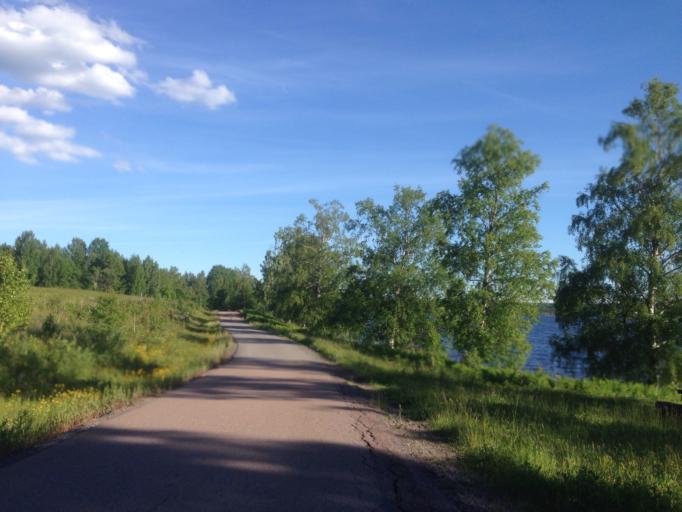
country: SE
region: Dalarna
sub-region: Ludvika Kommun
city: Ludvika
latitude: 60.1133
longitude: 15.2049
